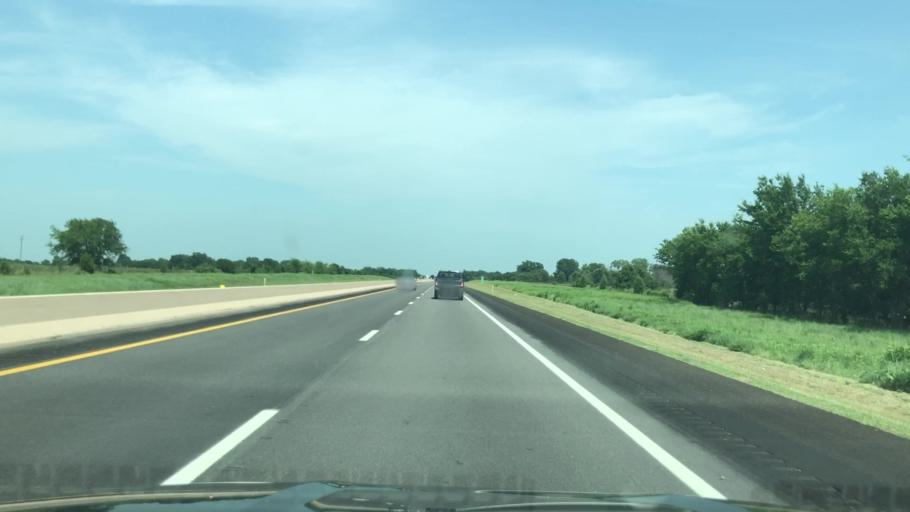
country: US
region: Oklahoma
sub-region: Craig County
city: Vinita
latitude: 36.6642
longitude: -95.0825
